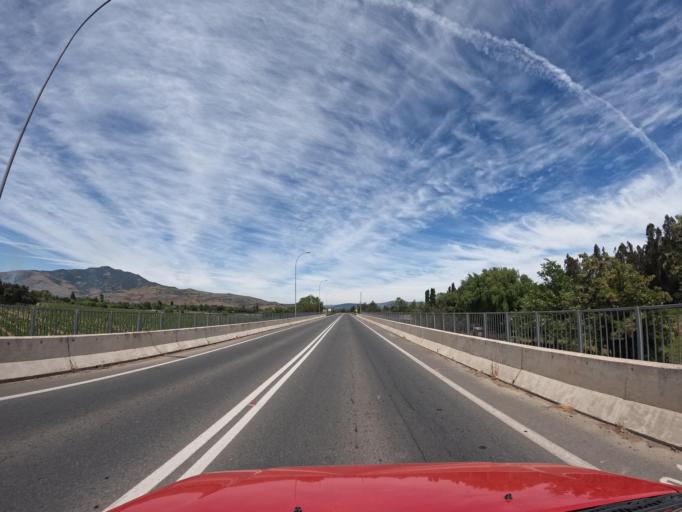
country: CL
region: Maule
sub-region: Provincia de Talca
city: Talca
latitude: -35.0938
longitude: -71.6461
